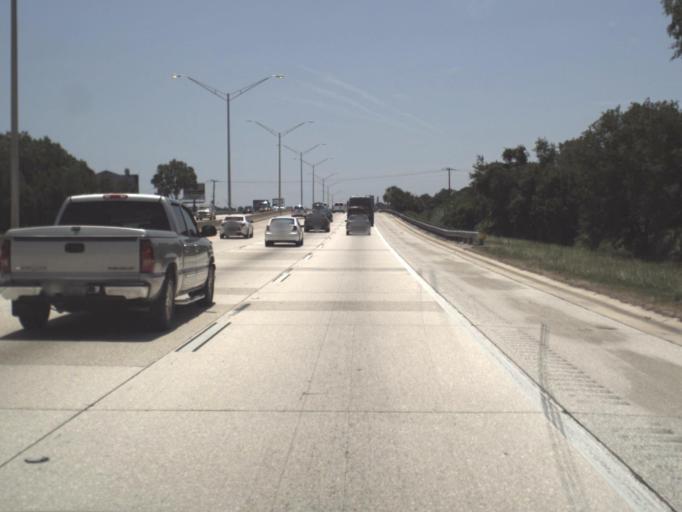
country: US
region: Florida
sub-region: Duval County
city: Jacksonville
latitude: 30.2669
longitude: -81.6105
